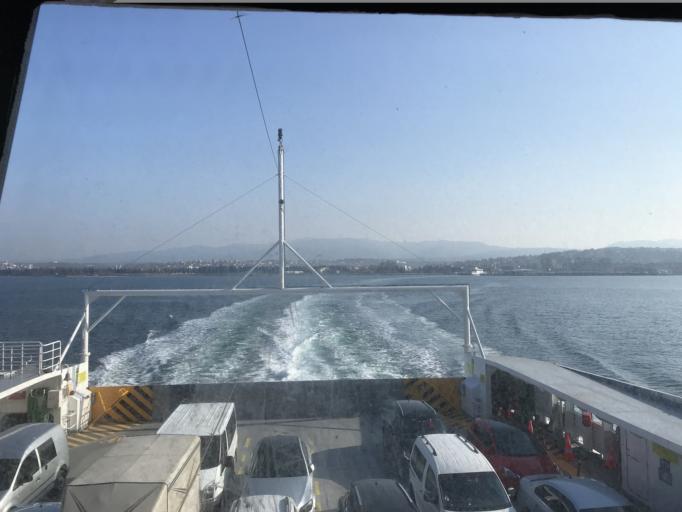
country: TR
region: Yalova
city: Yalova
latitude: 40.6710
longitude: 29.2750
